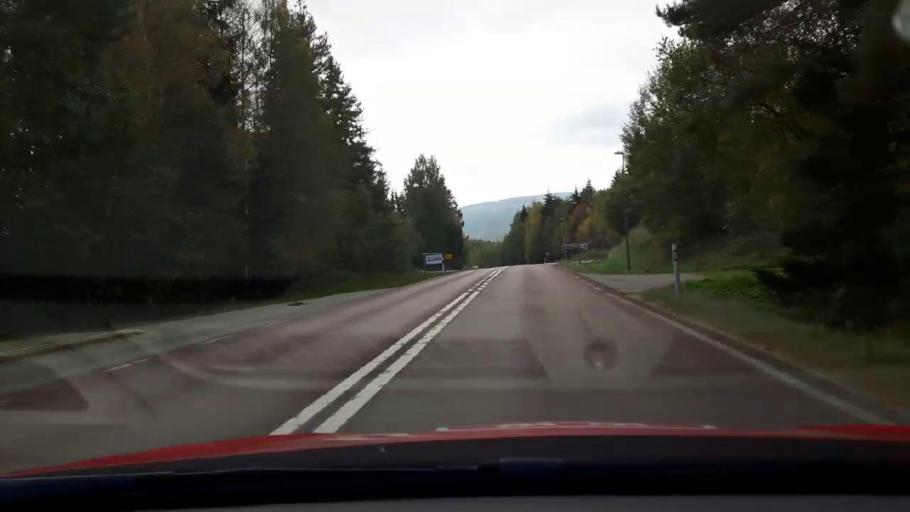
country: SE
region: Gaevleborg
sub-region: Ljusdals Kommun
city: Jaervsoe
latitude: 61.6851
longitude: 16.1469
